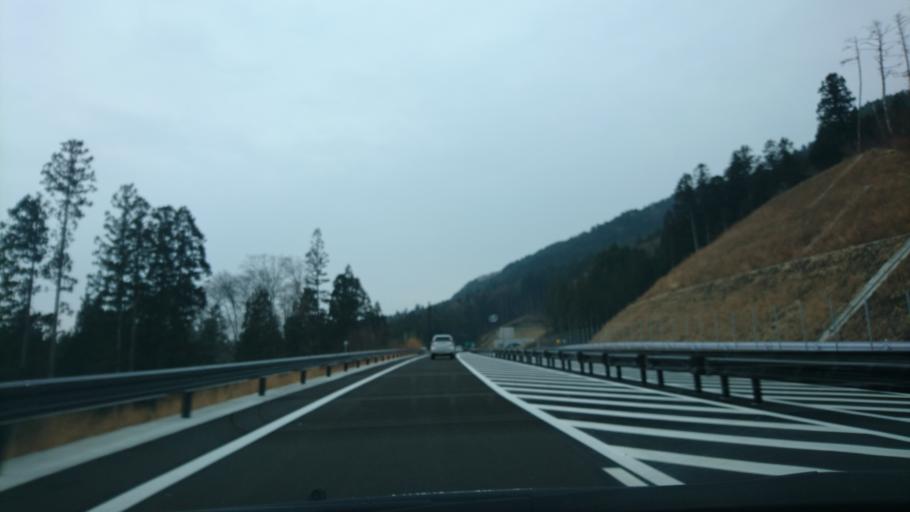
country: JP
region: Iwate
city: Ofunato
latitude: 38.9779
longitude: 141.6210
